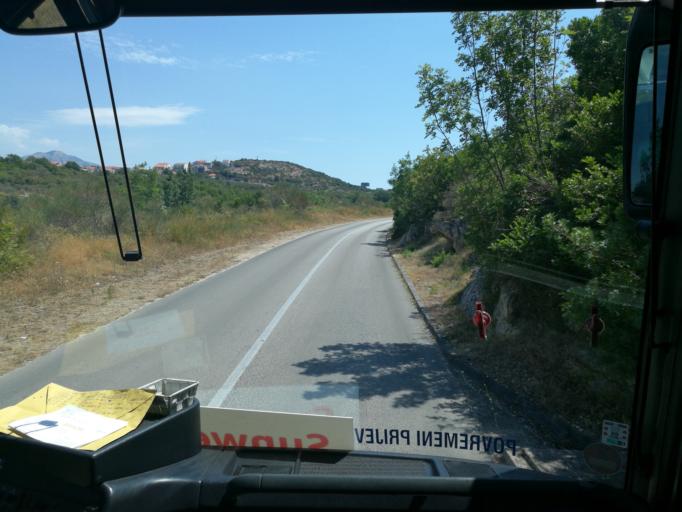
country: HR
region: Dubrovacko-Neretvanska
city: Cavtat
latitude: 42.5774
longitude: 18.2325
